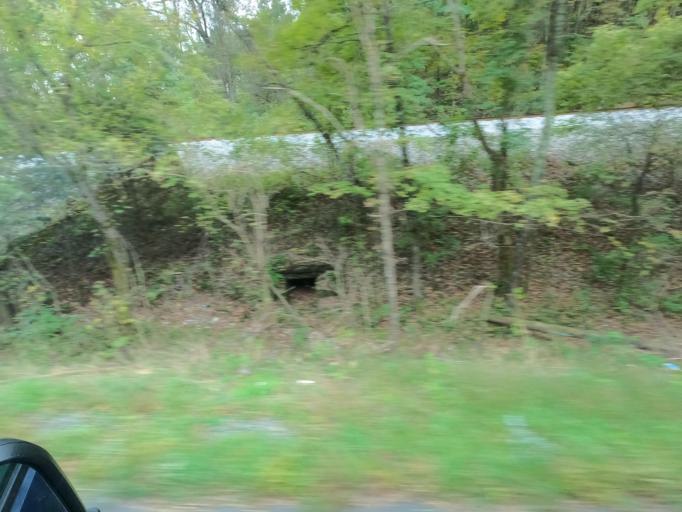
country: US
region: Tennessee
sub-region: Cheatham County
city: Pegram
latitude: 36.1071
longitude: -87.0662
